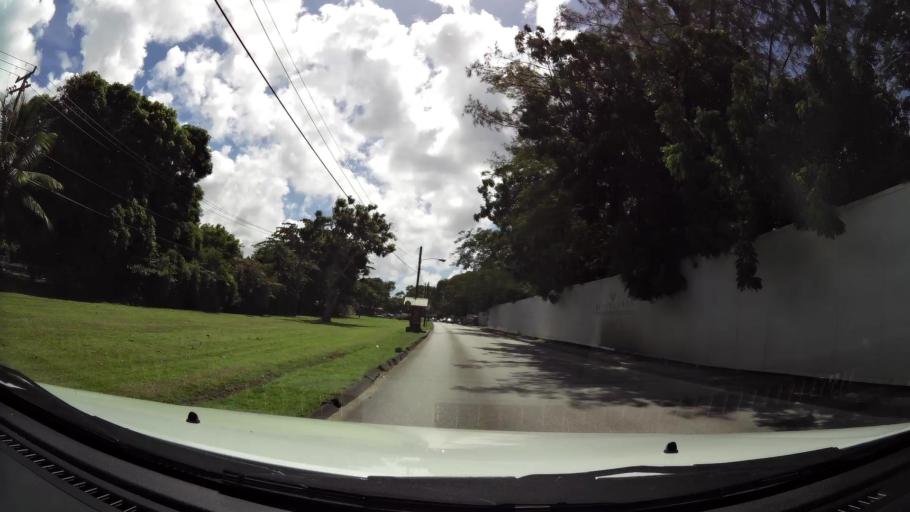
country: BB
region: Saint James
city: Holetown
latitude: 13.1798
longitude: -59.6386
